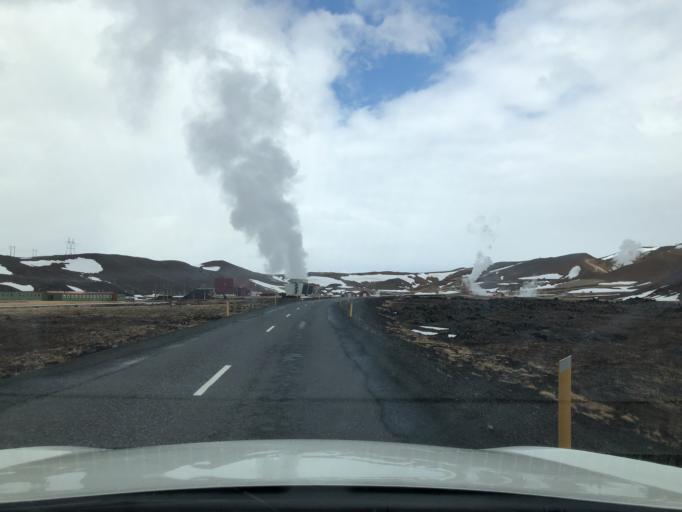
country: IS
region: Northeast
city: Laugar
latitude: 65.6968
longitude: -16.7740
